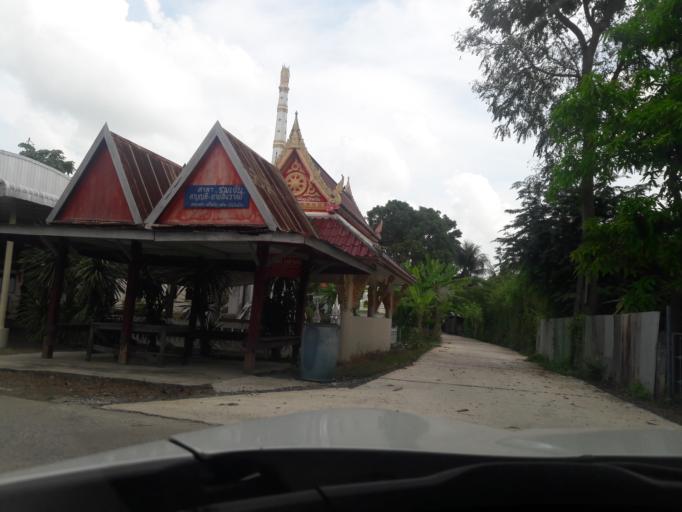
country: TH
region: Lop Buri
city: Ban Mi
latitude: 15.0467
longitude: 100.5496
